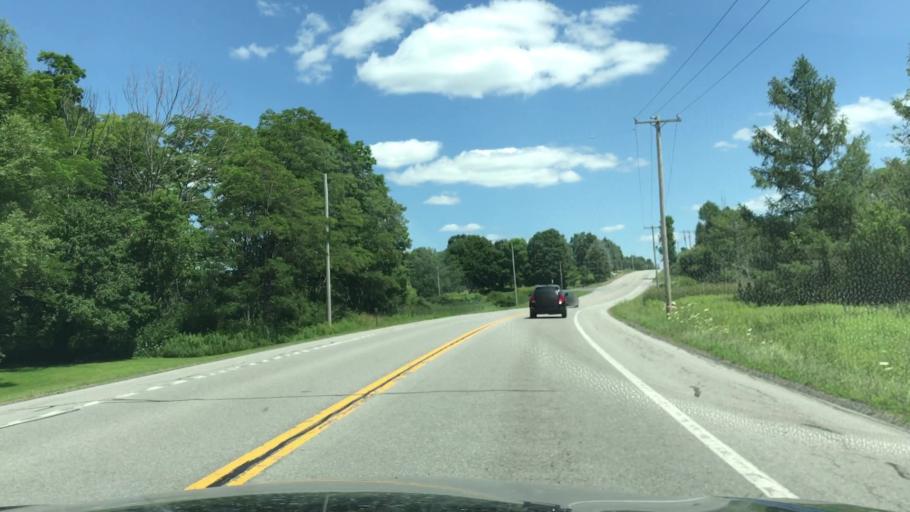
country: US
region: New York
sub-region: Wyoming County
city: Attica
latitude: 42.7563
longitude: -78.2809
